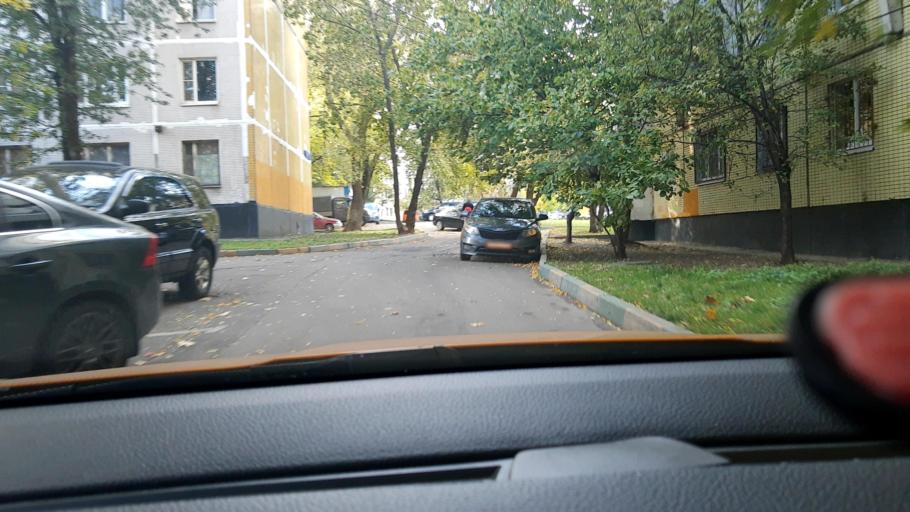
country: RU
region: Moscow
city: Orekhovo-Borisovo
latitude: 55.6099
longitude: 37.7417
